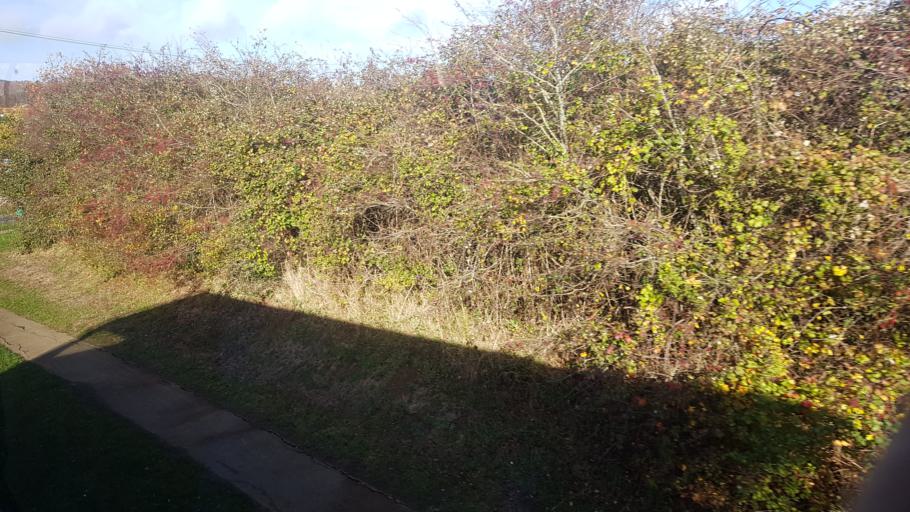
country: GB
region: England
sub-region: Isle of Wight
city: Shalfleet
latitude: 50.6448
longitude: -1.4004
